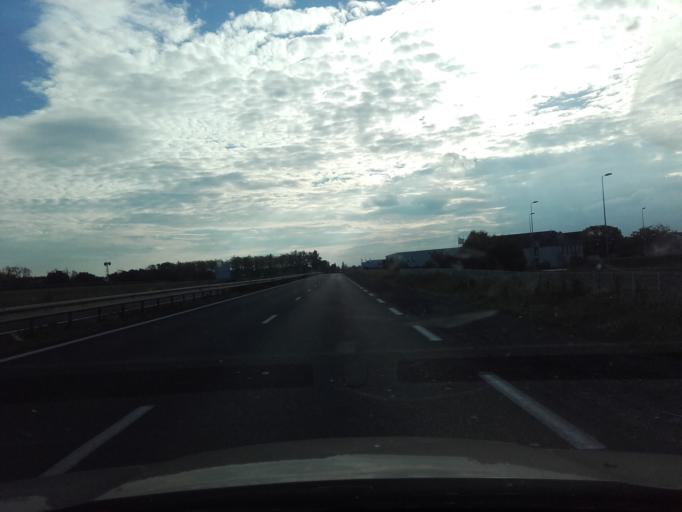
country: FR
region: Centre
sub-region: Departement d'Indre-et-Loire
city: Parcay-Meslay
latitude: 47.4464
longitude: 0.7243
